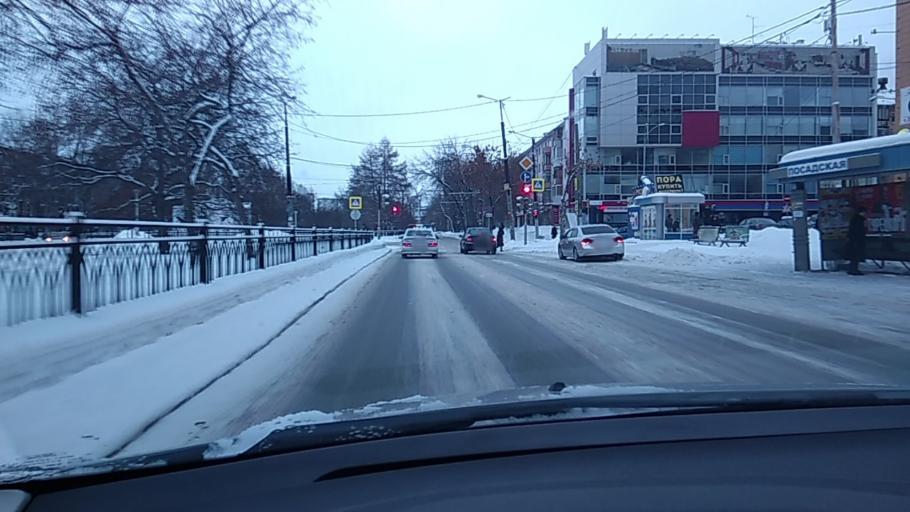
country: RU
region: Sverdlovsk
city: Yekaterinburg
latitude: 56.8206
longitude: 60.5770
